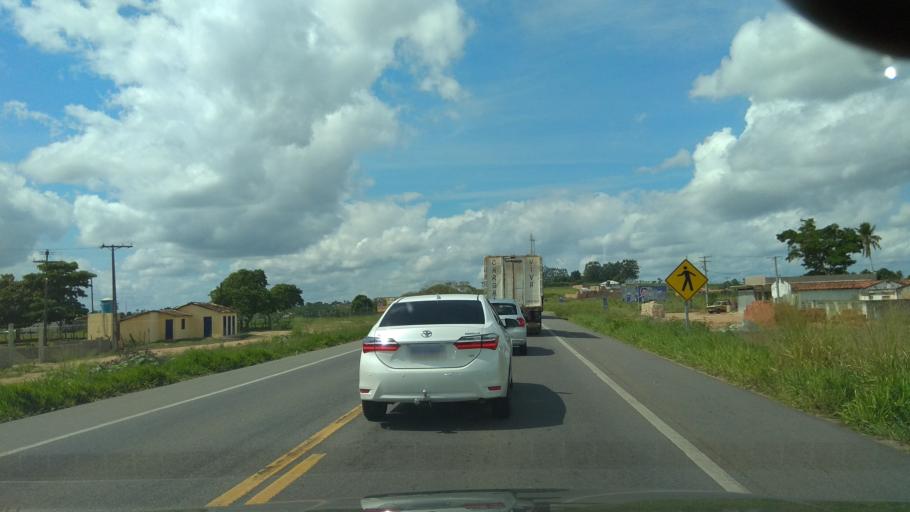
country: BR
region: Bahia
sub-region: Cruz Das Almas
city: Cruz das Almas
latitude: -12.6077
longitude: -39.0670
